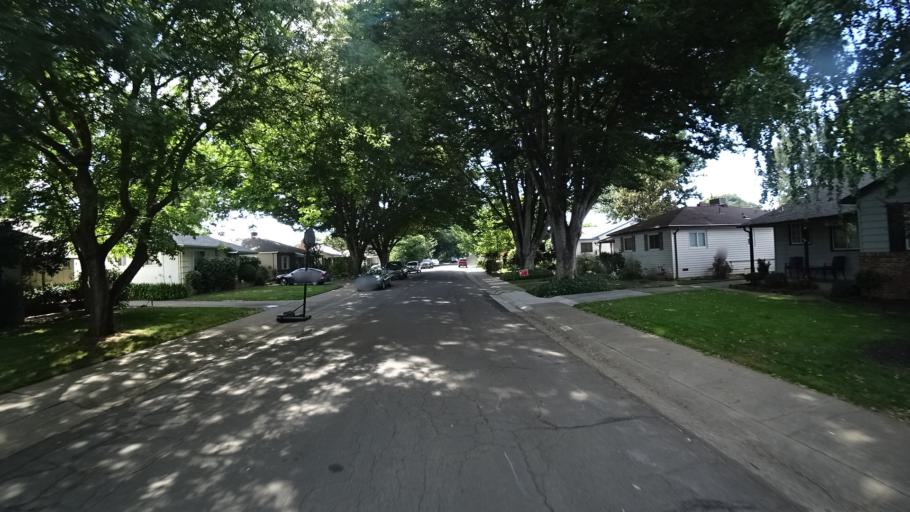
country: US
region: California
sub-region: Sacramento County
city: Arden-Arcade
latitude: 38.5782
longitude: -121.4325
